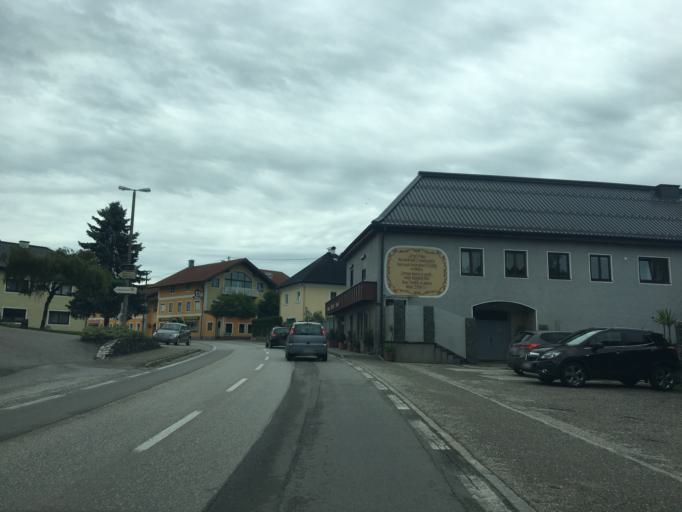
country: AT
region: Salzburg
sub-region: Politischer Bezirk Salzburg-Umgebung
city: Dorfbeuern
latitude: 48.0449
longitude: 12.9894
